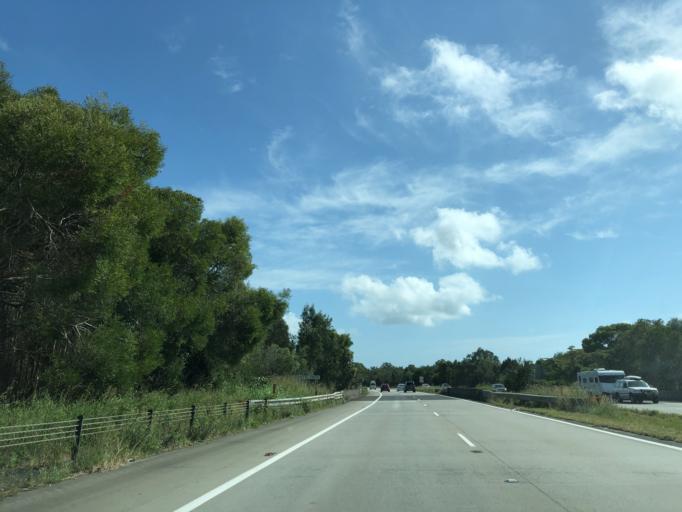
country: AU
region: New South Wales
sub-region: Byron Shire
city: Brunswick Heads
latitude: -28.5657
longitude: 153.5415
